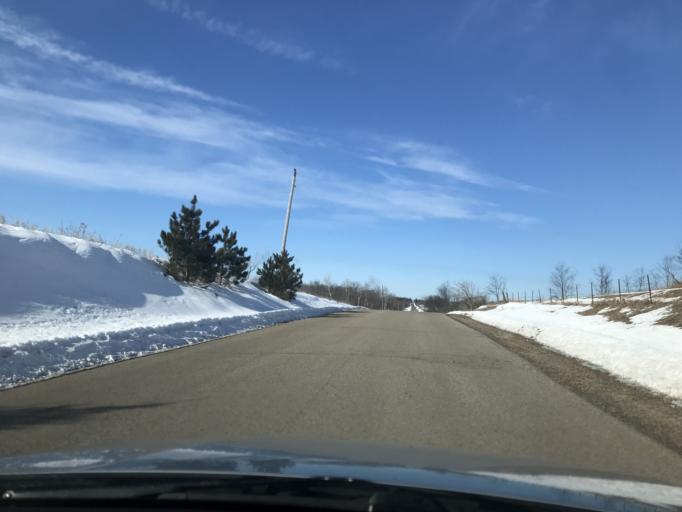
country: US
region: Wisconsin
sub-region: Oconto County
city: Gillett
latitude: 44.9394
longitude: -88.2391
